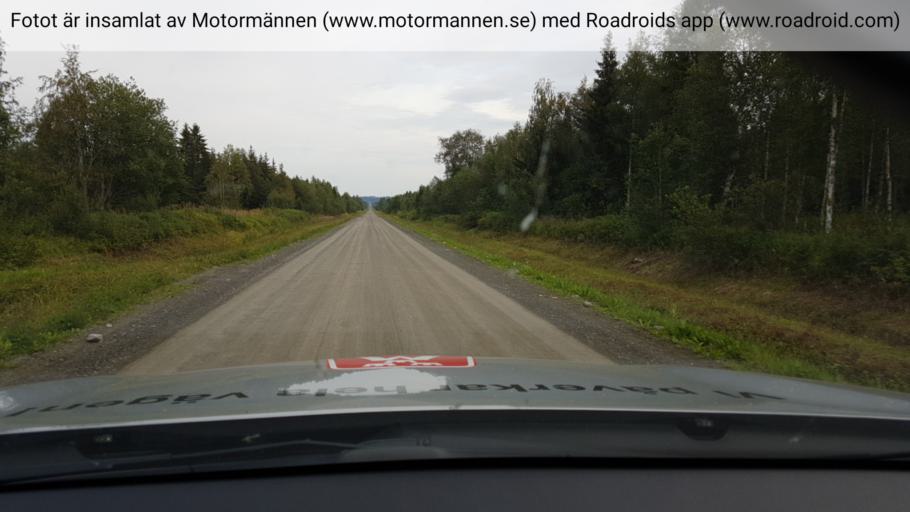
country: SE
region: Jaemtland
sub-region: OEstersunds Kommun
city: Lit
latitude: 63.6791
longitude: 14.8634
